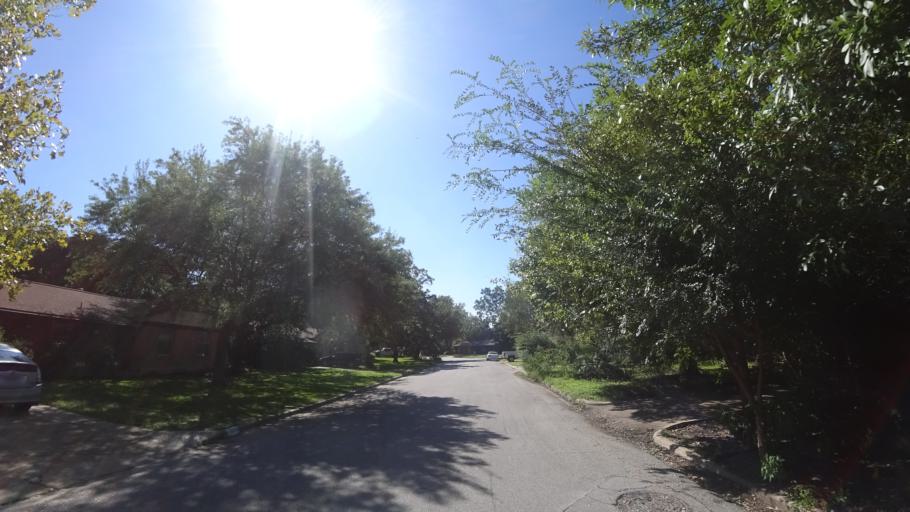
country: US
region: Texas
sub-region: Travis County
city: Austin
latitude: 30.3181
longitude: -97.6938
